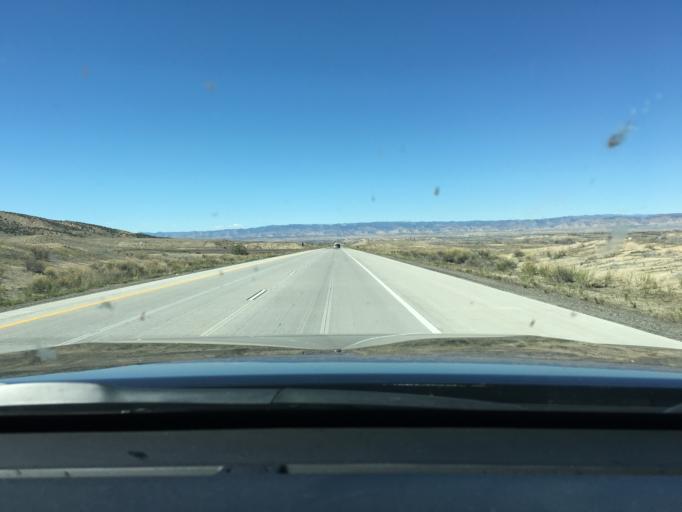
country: US
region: Colorado
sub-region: Mesa County
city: Loma
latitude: 39.2049
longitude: -108.8558
